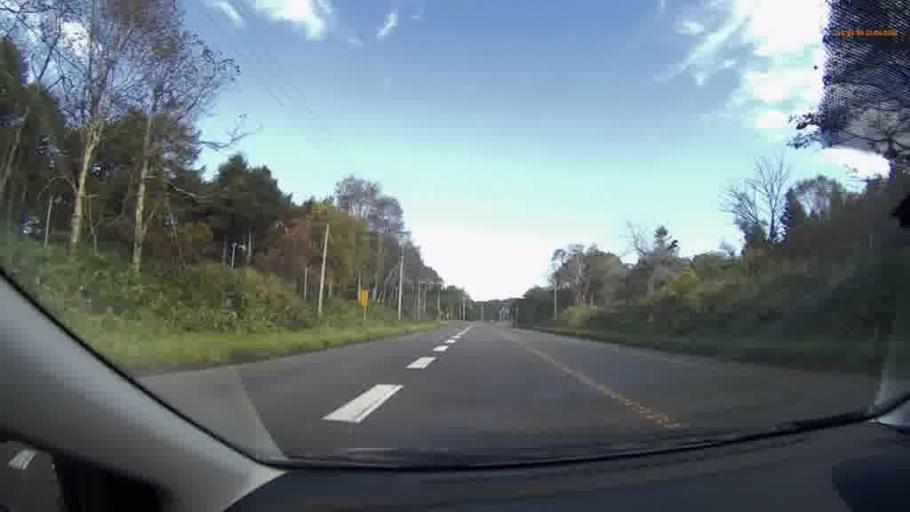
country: JP
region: Hokkaido
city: Kushiro
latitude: 42.9305
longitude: 144.0148
